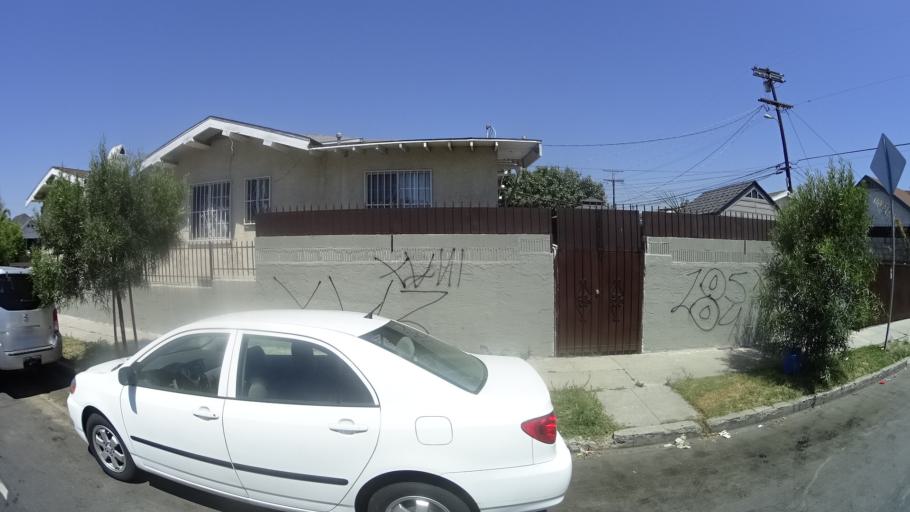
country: US
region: California
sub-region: Los Angeles County
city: View Park-Windsor Hills
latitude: 33.9947
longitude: -118.2958
